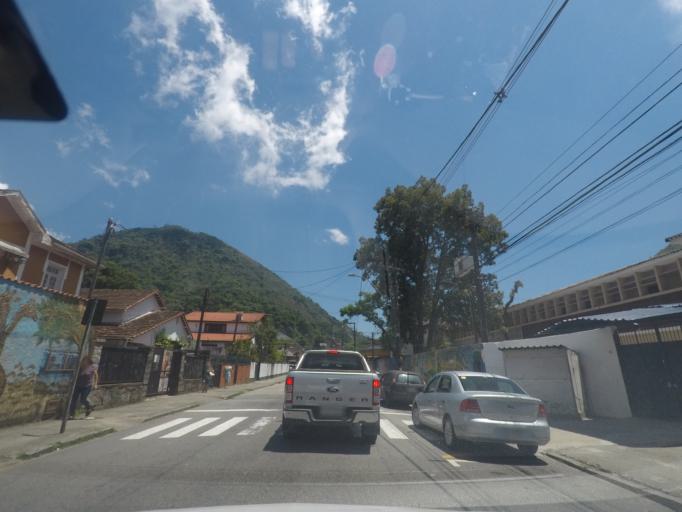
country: BR
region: Rio de Janeiro
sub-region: Petropolis
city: Petropolis
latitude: -22.5285
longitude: -43.1728
